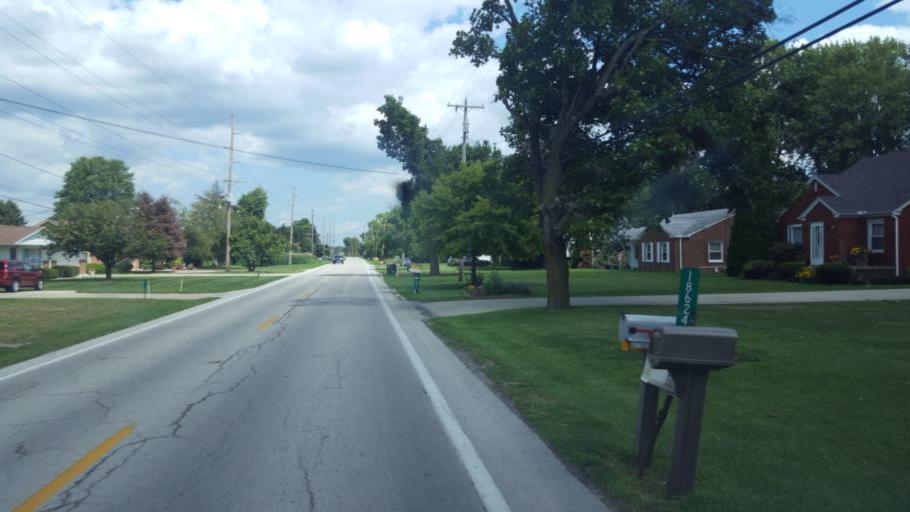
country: US
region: Ohio
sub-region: Ottawa County
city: Elmore
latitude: 41.4808
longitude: -83.2922
